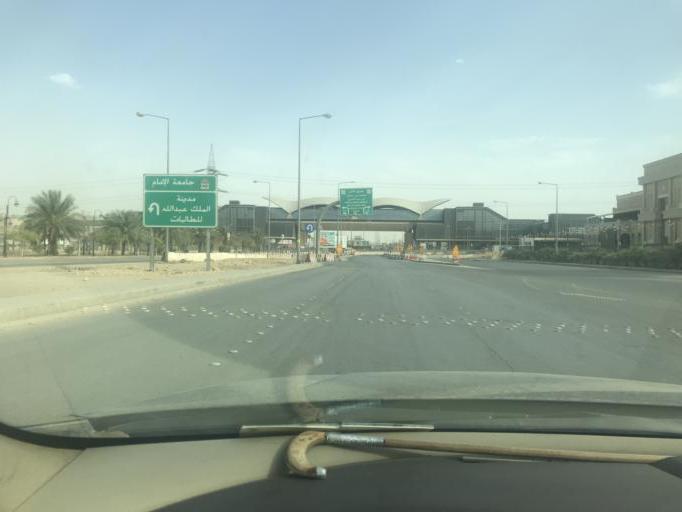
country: SA
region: Ar Riyad
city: Riyadh
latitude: 24.8036
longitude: 46.6949
